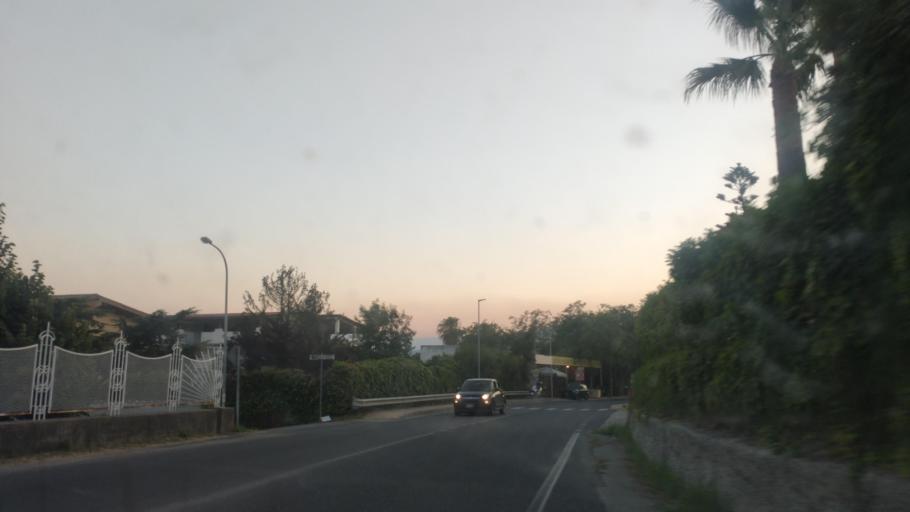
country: IT
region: Calabria
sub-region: Provincia di Catanzaro
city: Montepaone Lido
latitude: 38.7429
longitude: 16.5521
